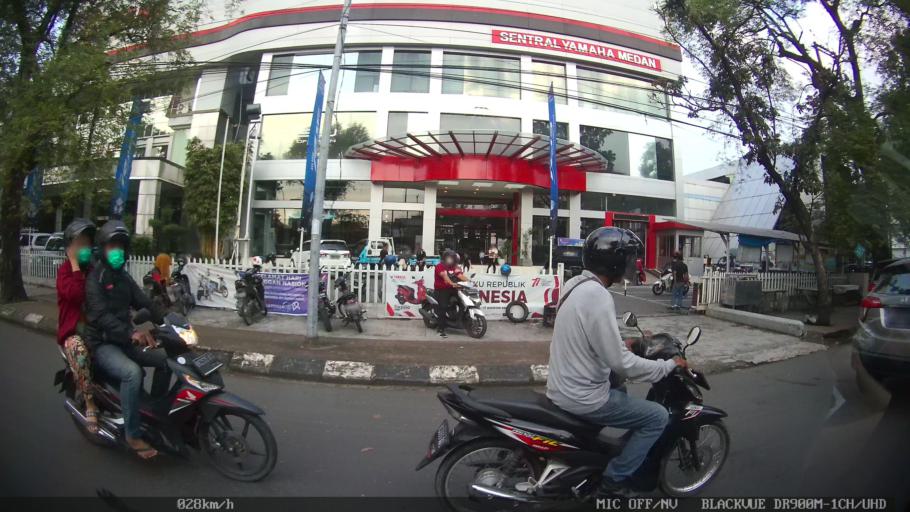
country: ID
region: North Sumatra
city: Medan
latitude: 3.5982
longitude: 98.6692
